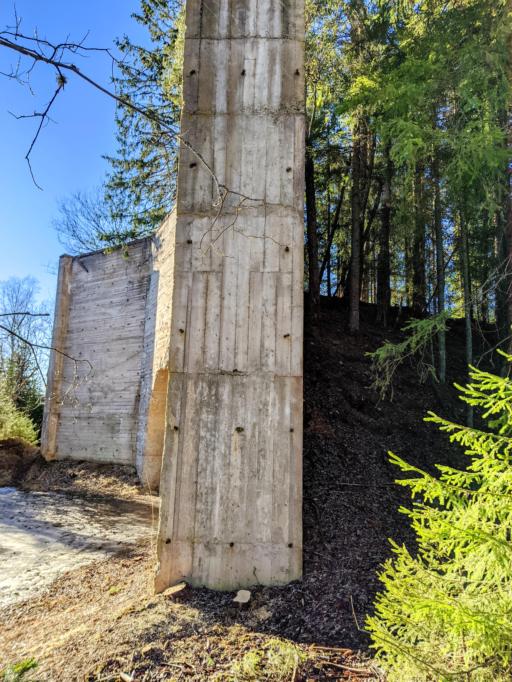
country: NO
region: Akershus
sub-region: Eidsvoll
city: Raholt
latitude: 60.2212
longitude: 11.1176
